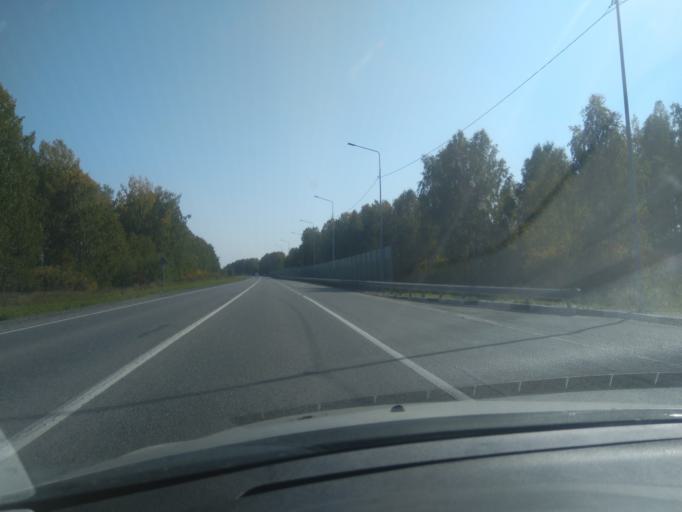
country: RU
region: Sverdlovsk
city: Sovkhoznyy
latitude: 56.5186
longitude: 61.4412
